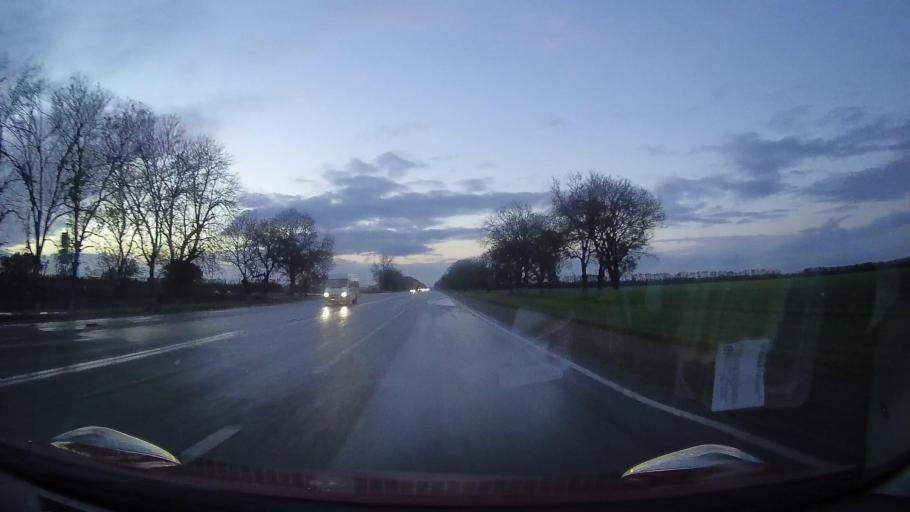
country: RU
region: Krasnodarskiy
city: Zavetnyy
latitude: 44.8865
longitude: 41.2160
